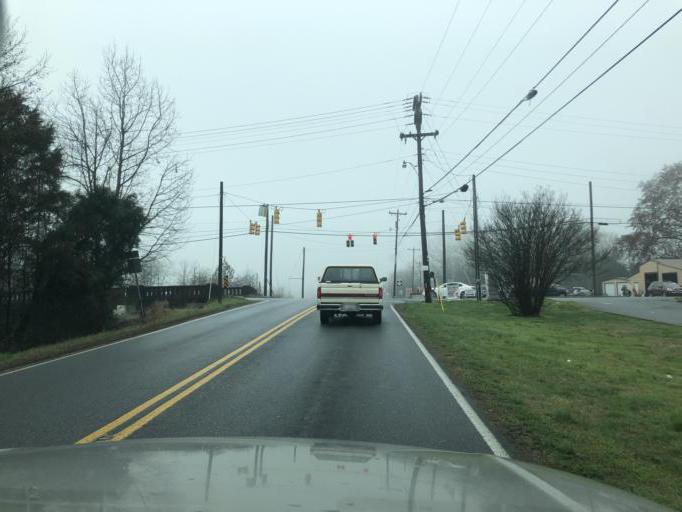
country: US
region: North Carolina
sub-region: Gaston County
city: Cherryville
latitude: 35.3619
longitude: -81.4280
